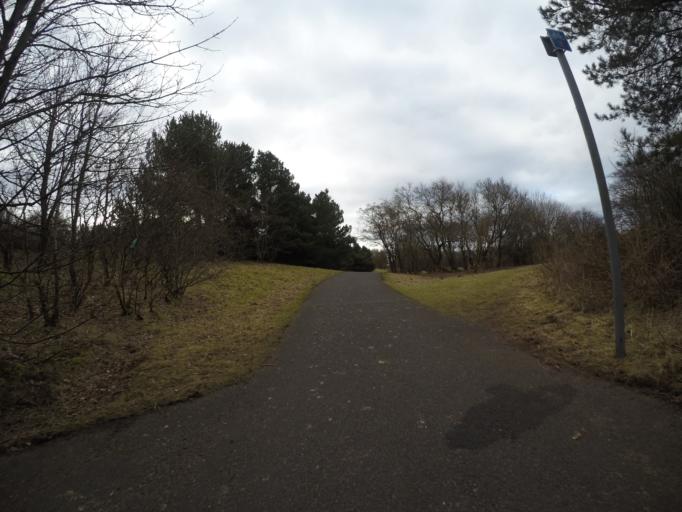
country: GB
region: Scotland
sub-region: North Ayrshire
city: Irvine
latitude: 55.6050
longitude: -4.6807
